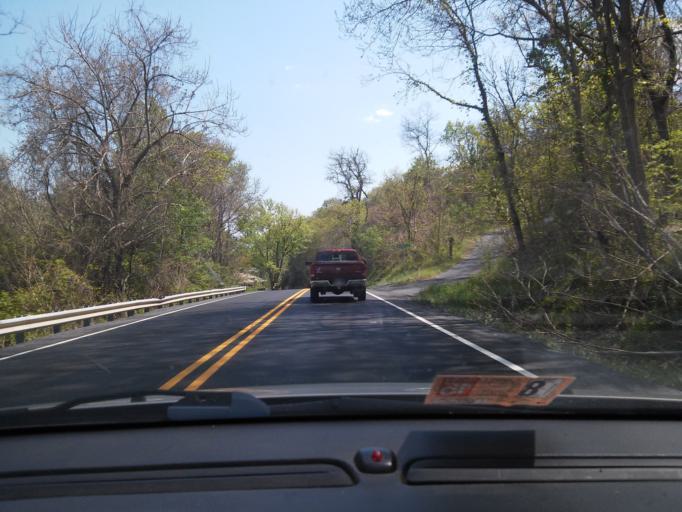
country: US
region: Virginia
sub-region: Warren County
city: Apple Mountain Lake
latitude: 38.8537
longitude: -78.1281
